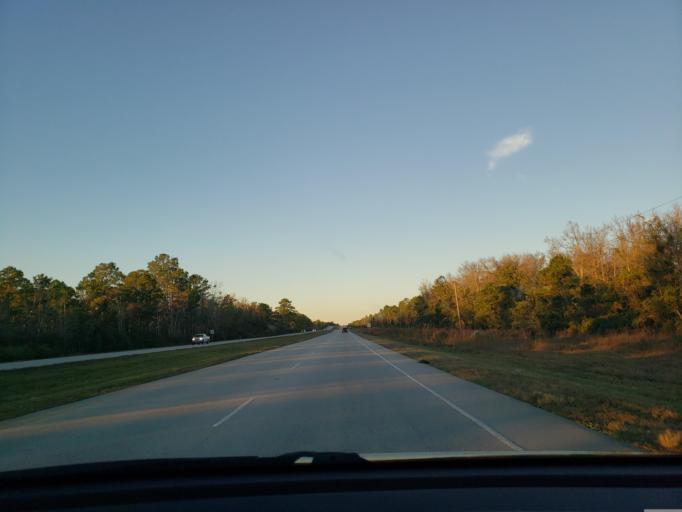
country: US
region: North Carolina
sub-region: Onslow County
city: Sneads Ferry
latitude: 34.6257
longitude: -77.4823
